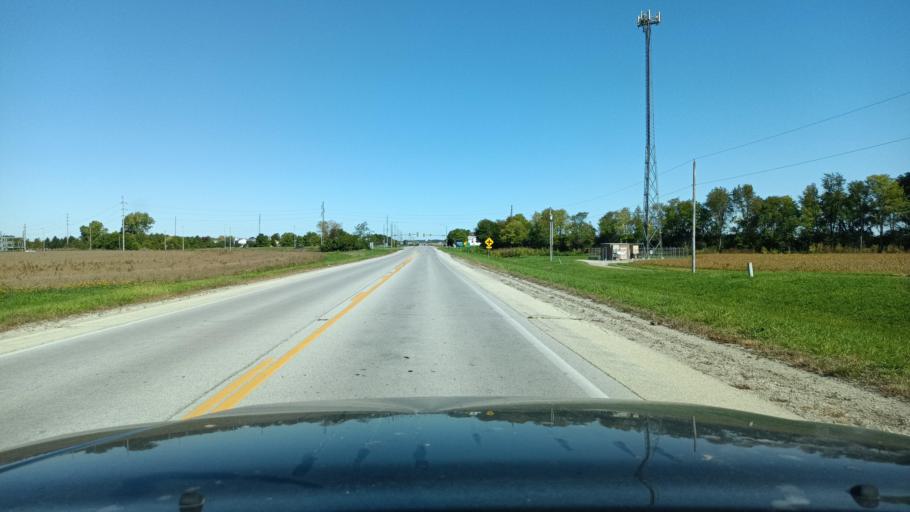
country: US
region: Illinois
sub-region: Champaign County
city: Urbana
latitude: 40.0809
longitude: -88.1621
